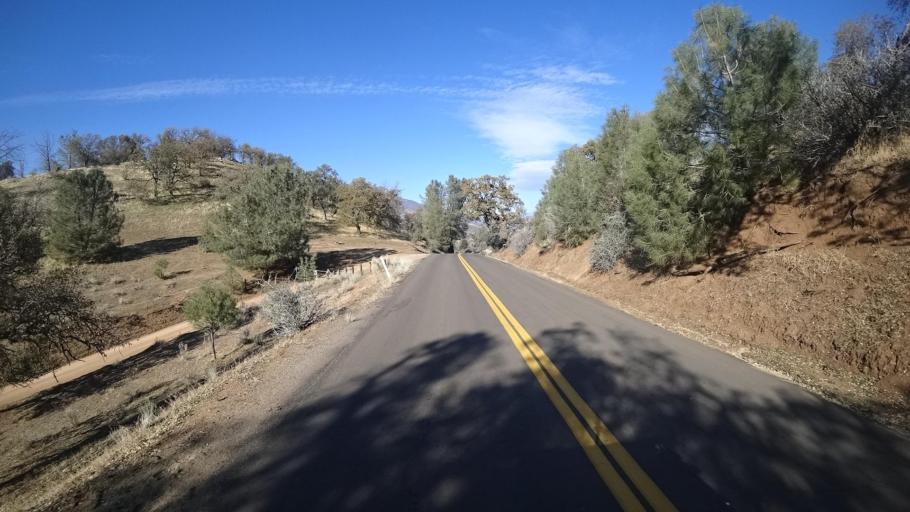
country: US
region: California
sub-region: Kern County
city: Bear Valley Springs
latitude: 35.3662
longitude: -118.5576
